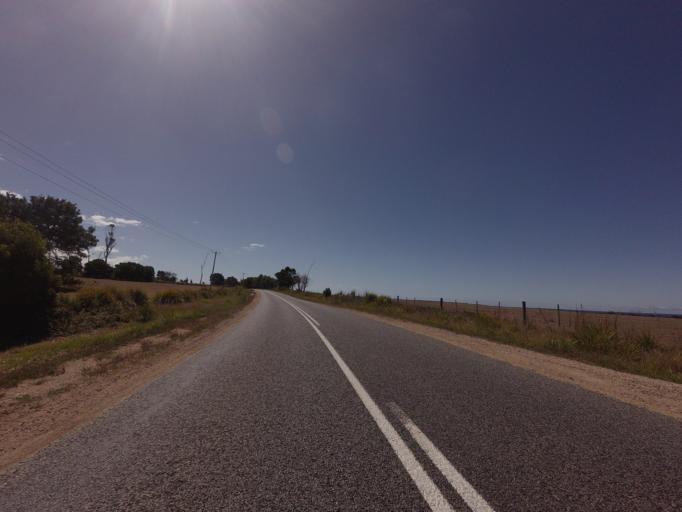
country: AU
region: Tasmania
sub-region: Break O'Day
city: St Helens
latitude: -41.7710
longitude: 148.2693
